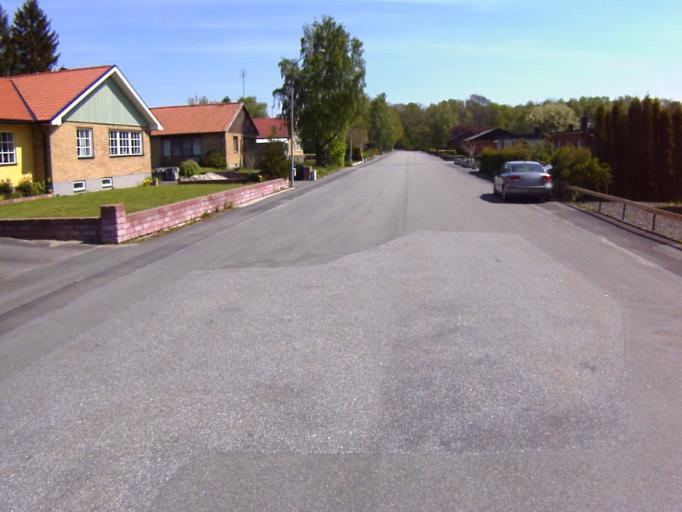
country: SE
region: Skane
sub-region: Kristianstads Kommun
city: Onnestad
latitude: 55.9307
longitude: 13.9863
